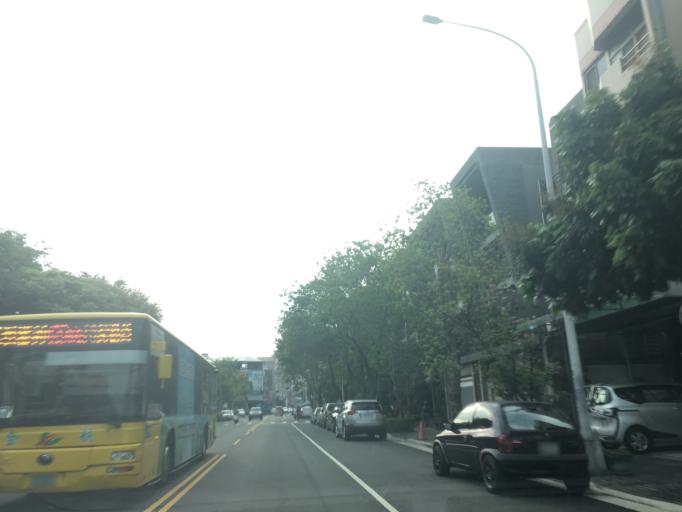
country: TW
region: Taiwan
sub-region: Taichung City
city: Taichung
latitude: 24.1944
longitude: 120.6806
